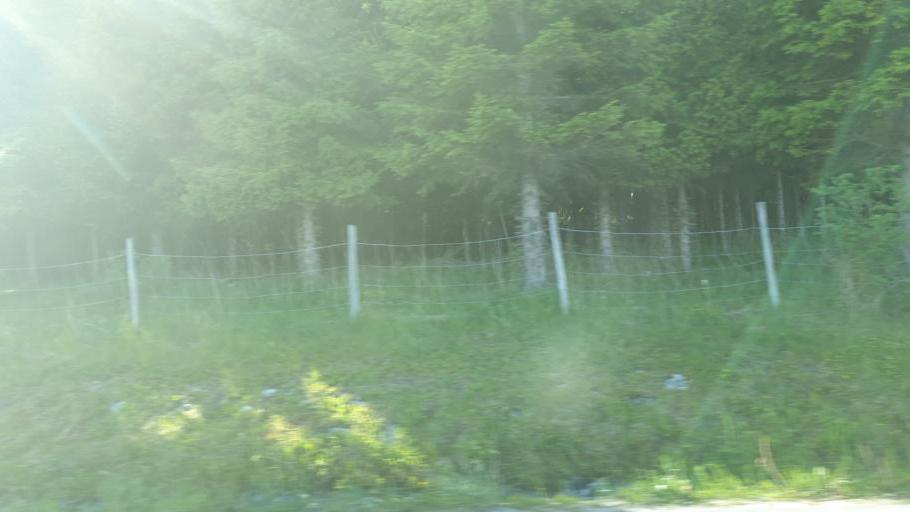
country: NO
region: Sor-Trondelag
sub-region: Skaun
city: Borsa
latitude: 63.5023
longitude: 10.1259
